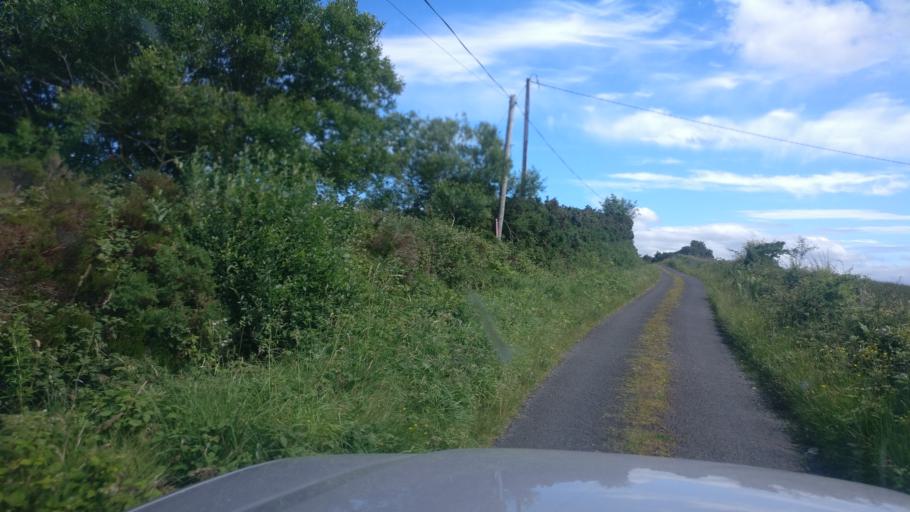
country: IE
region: Connaught
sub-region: County Galway
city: Gort
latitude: 53.0724
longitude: -8.7062
